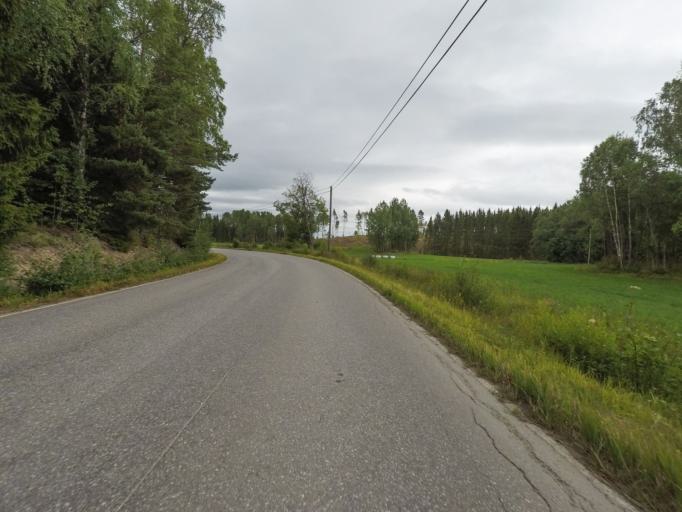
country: FI
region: Uusimaa
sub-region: Helsinki
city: Karjalohja
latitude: 60.2608
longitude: 23.6946
